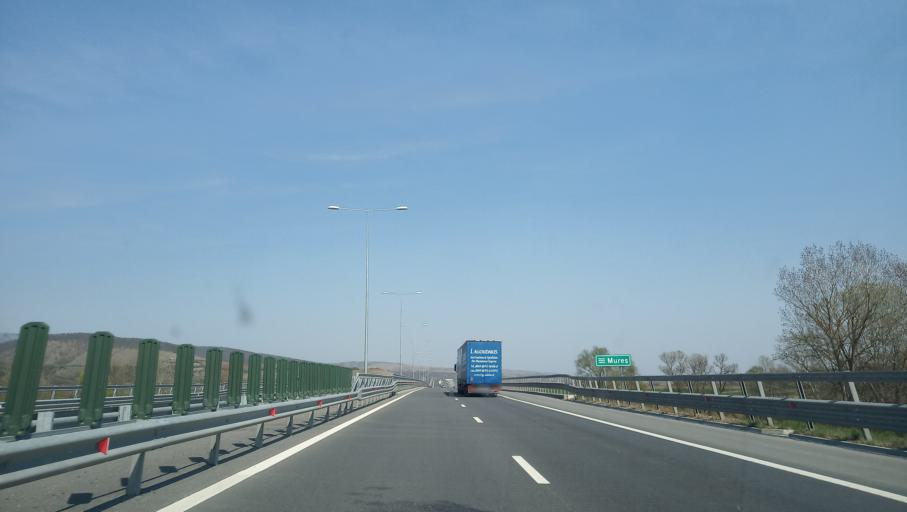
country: RO
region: Alba
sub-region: Comuna Miraslau
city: Miraslau
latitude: 46.3644
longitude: 23.7346
